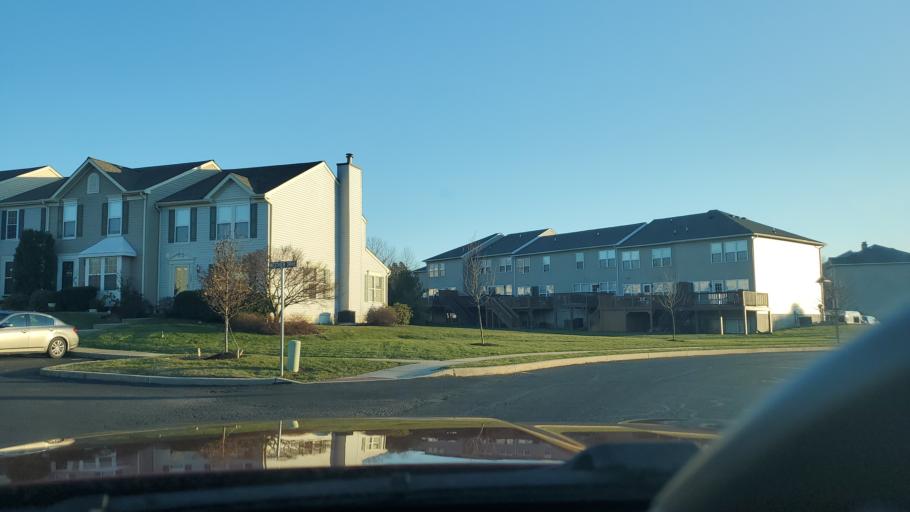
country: US
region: Pennsylvania
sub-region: Montgomery County
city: Woxall
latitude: 40.3057
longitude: -75.4907
